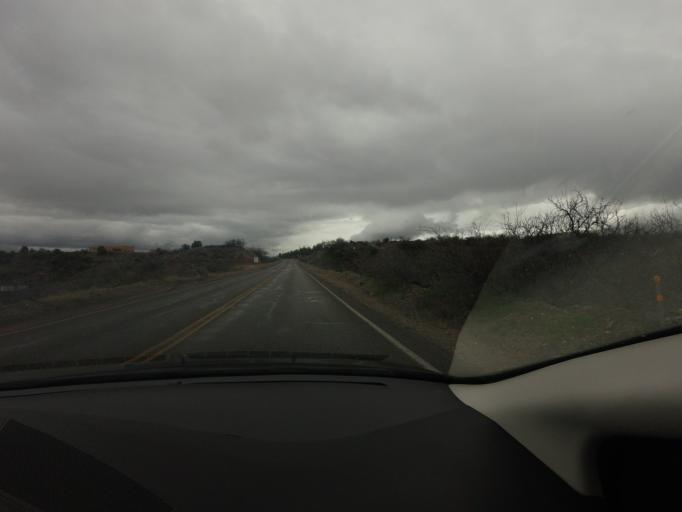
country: US
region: Arizona
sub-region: Yavapai County
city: Clarkdale
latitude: 34.7558
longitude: -112.0367
